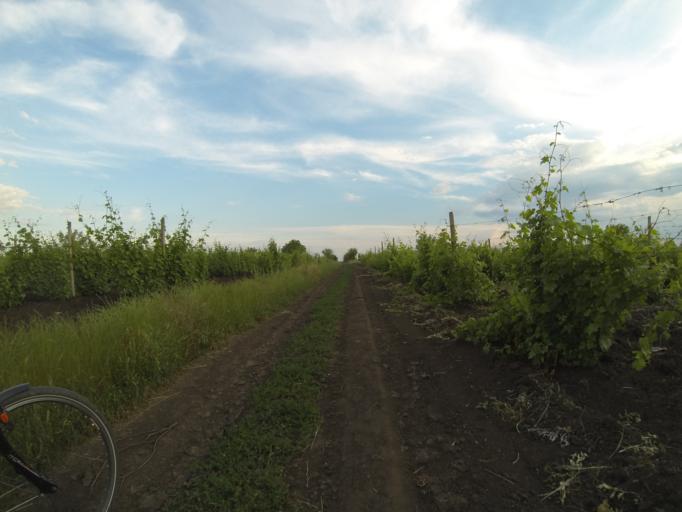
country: RO
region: Dolj
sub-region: Comuna Ceratu
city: Ceratu
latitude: 44.1128
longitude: 23.6822
